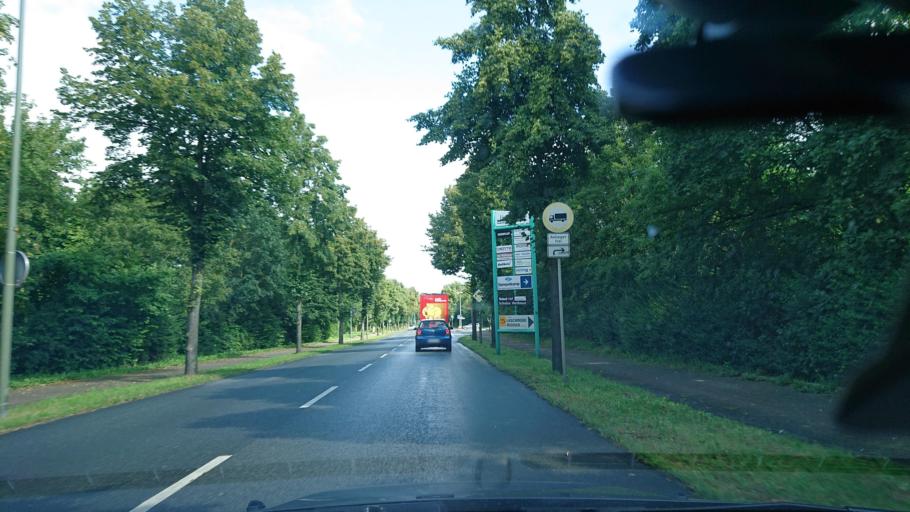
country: DE
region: North Rhine-Westphalia
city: Lunen
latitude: 51.6175
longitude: 7.5438
